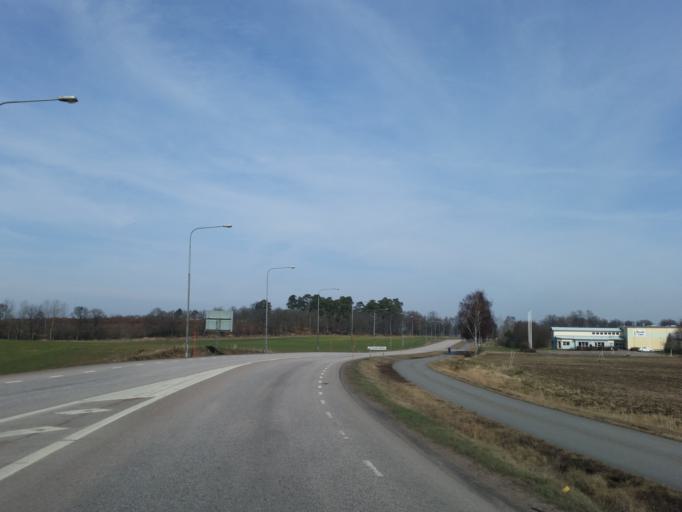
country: SE
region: Kalmar
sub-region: Kalmar Kommun
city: Rinkabyholm
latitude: 56.6737
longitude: 16.3025
